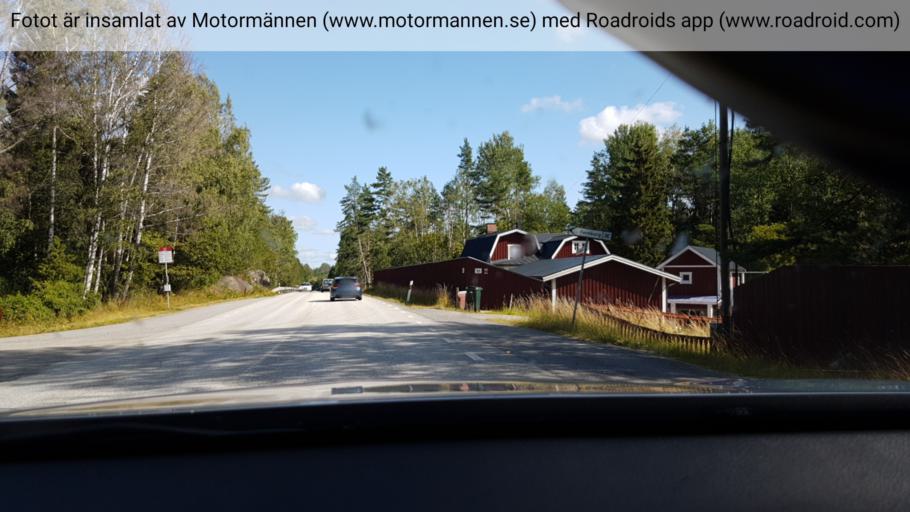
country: SE
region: Stockholm
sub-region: Norrtalje Kommun
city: Norrtalje
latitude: 59.7250
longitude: 18.6777
